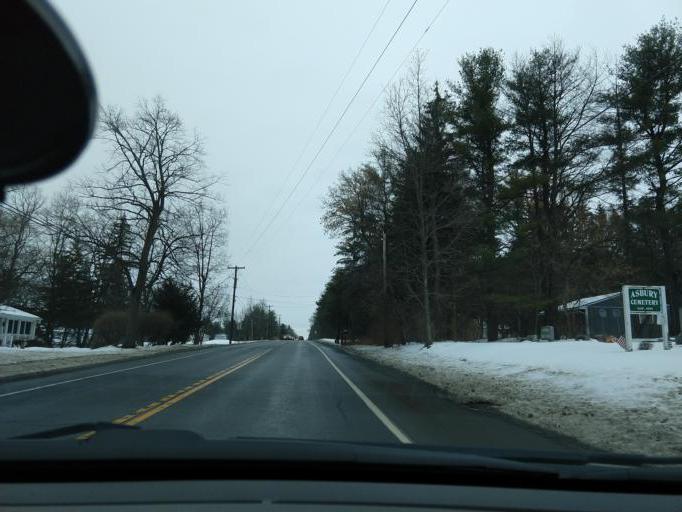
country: US
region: New York
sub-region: Tompkins County
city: Lansing
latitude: 42.5269
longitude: -76.4918
